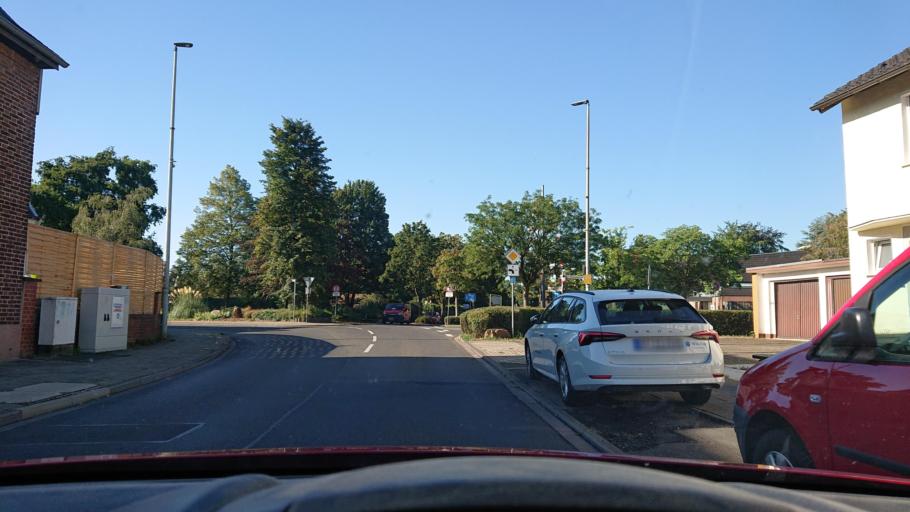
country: DE
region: North Rhine-Westphalia
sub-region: Regierungsbezirk Koln
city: Bergheim
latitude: 50.9740
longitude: 6.6778
